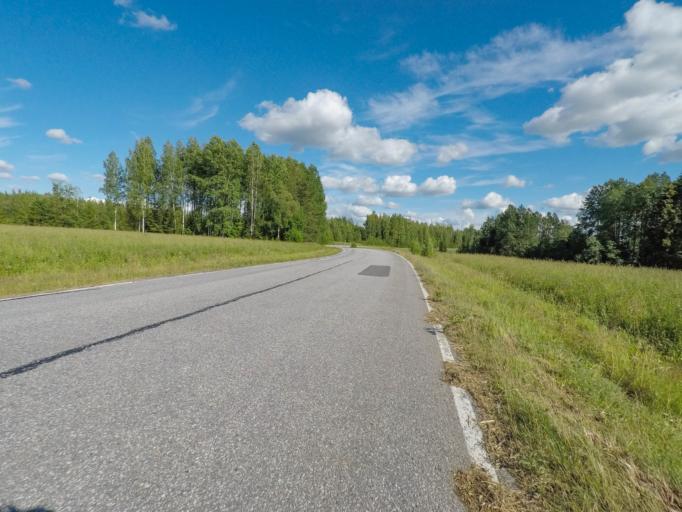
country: FI
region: South Karelia
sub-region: Imatra
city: Imatra
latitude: 61.1350
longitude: 28.6573
